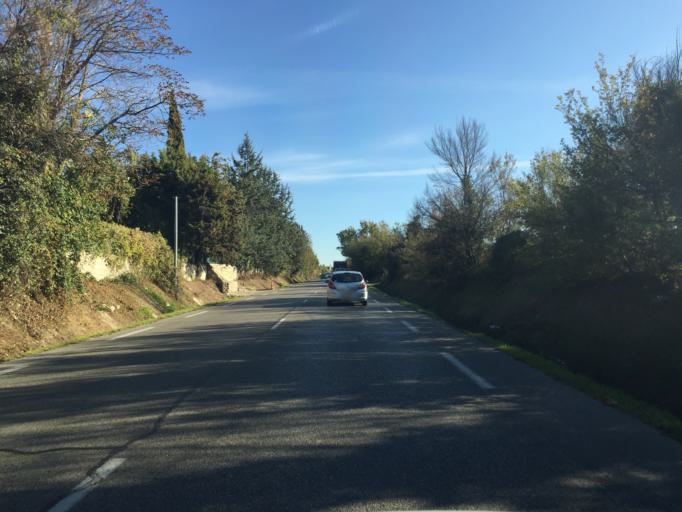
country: FR
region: Provence-Alpes-Cote d'Azur
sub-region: Departement des Bouches-du-Rhone
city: Aix-en-Provence
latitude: 43.5609
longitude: 5.4112
